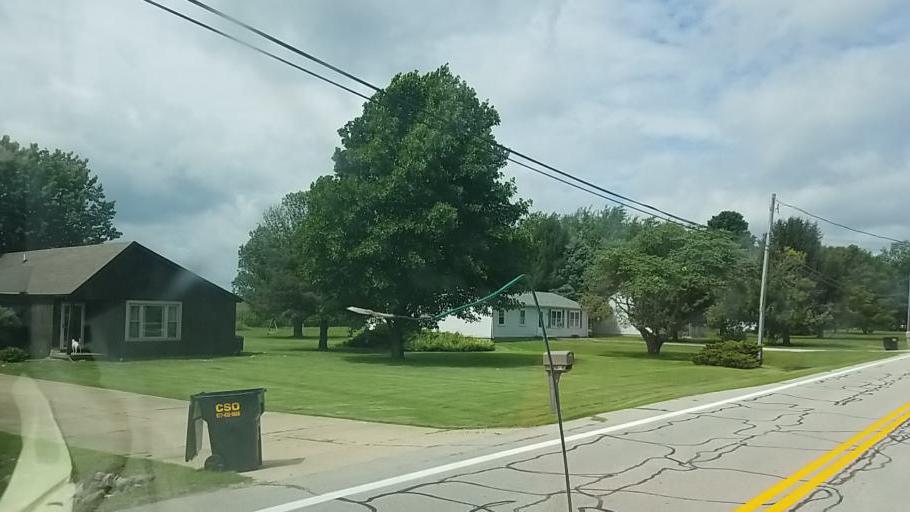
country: US
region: Ohio
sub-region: Fayette County
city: Jeffersonville
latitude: 39.6580
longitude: -83.5675
